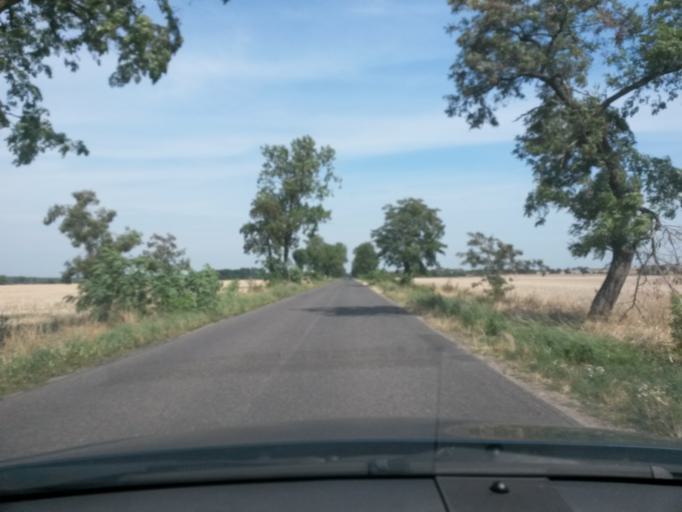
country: PL
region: Lower Silesian Voivodeship
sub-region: Powiat legnicki
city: Prochowice
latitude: 51.2050
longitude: 16.3472
